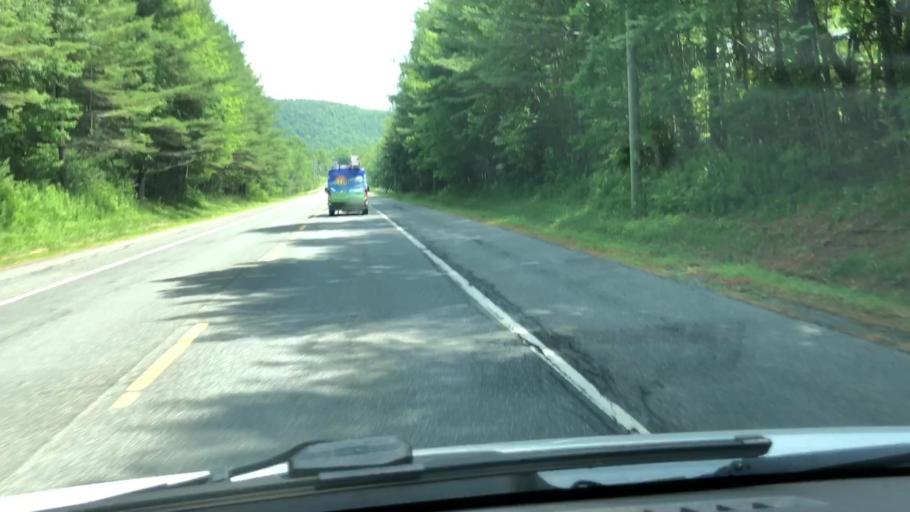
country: US
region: Massachusetts
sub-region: Berkshire County
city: Hinsdale
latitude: 42.4877
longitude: -72.9926
